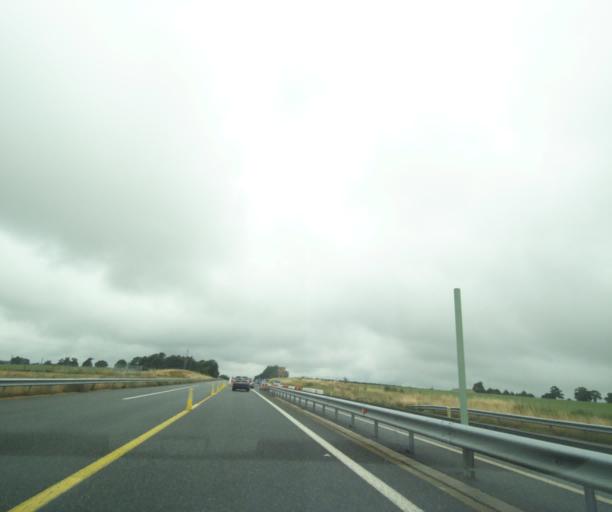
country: FR
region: Midi-Pyrenees
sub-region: Departement de l'Aveyron
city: Luc-la-Primaube
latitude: 44.2951
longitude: 2.5214
